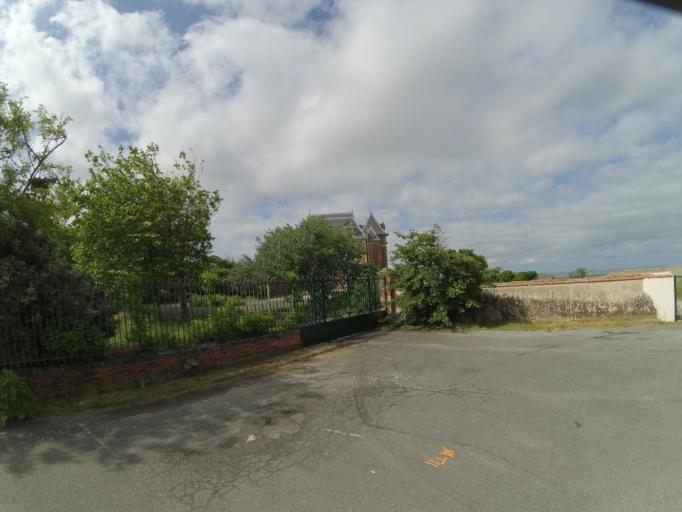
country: FR
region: Poitou-Charentes
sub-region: Departement de la Charente-Maritime
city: Angoulins
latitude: 46.0970
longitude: -1.1040
